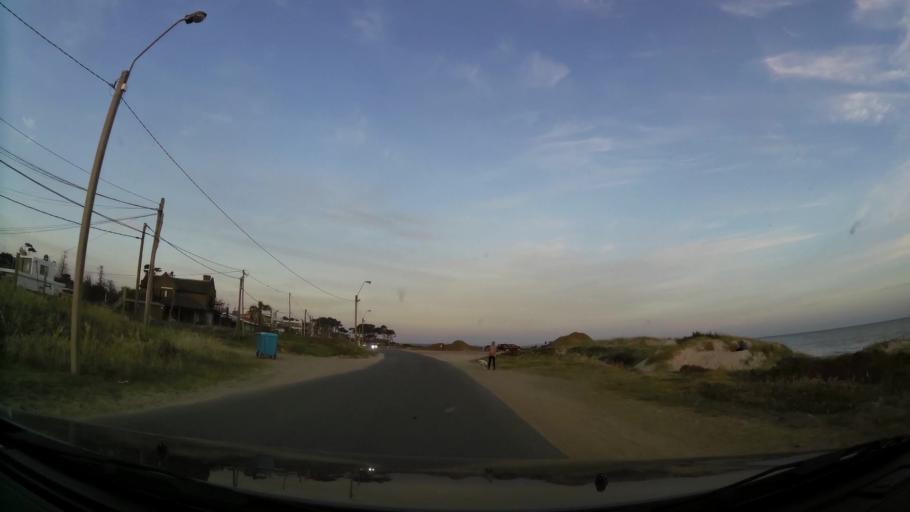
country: UY
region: Canelones
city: Atlantida
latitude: -34.7796
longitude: -55.7507
